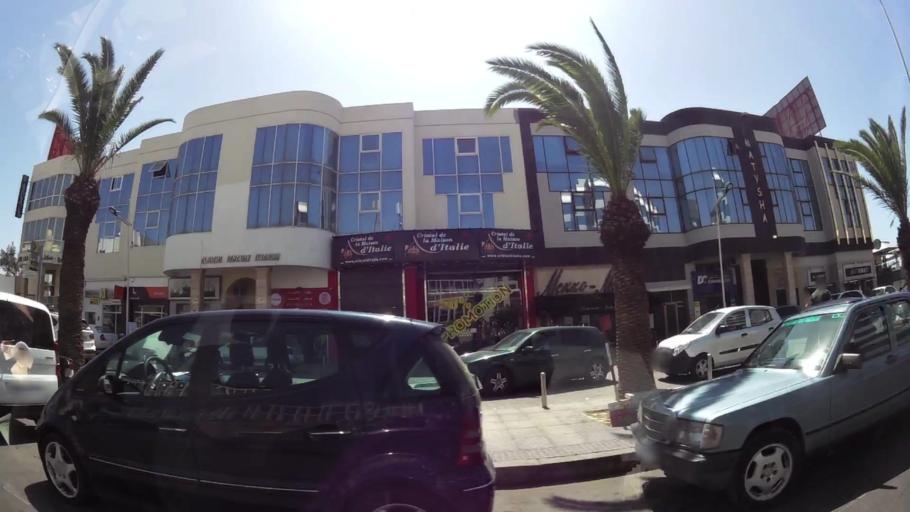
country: MA
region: Souss-Massa-Draa
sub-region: Agadir-Ida-ou-Tnan
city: Agadir
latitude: 30.4161
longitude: -9.5952
